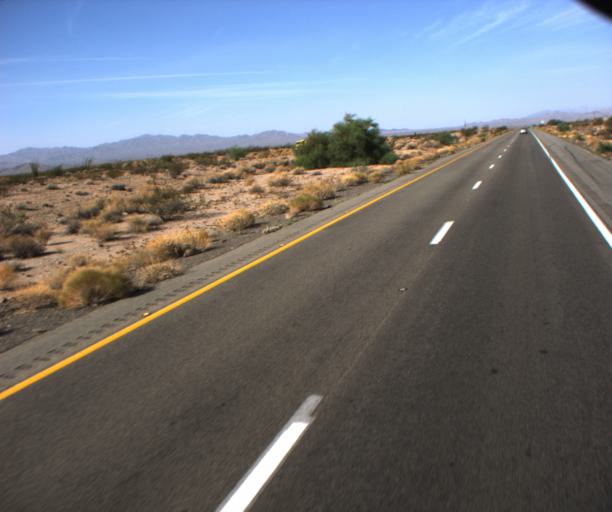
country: US
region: Arizona
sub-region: Mohave County
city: Desert Hills
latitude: 34.7922
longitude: -114.1647
